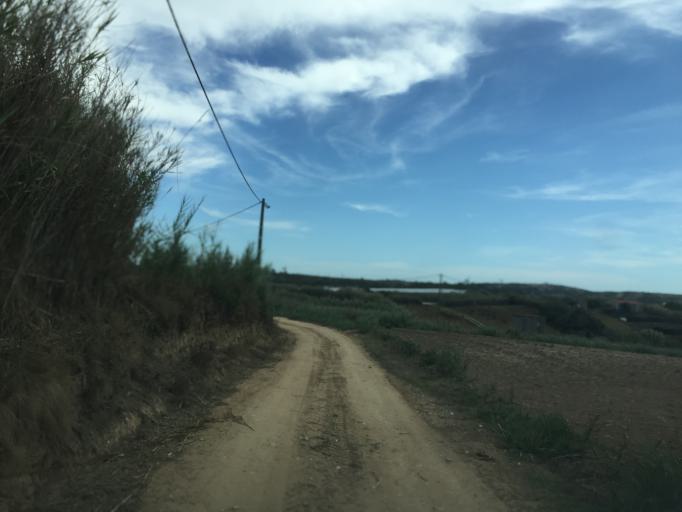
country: PT
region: Lisbon
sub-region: Lourinha
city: Lourinha
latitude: 39.1884
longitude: -9.3431
